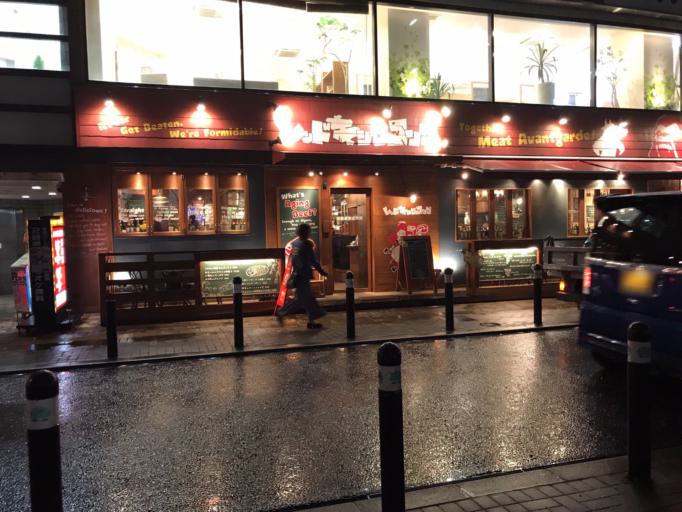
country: JP
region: Tokyo
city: Hachioji
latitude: 35.5950
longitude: 139.3464
